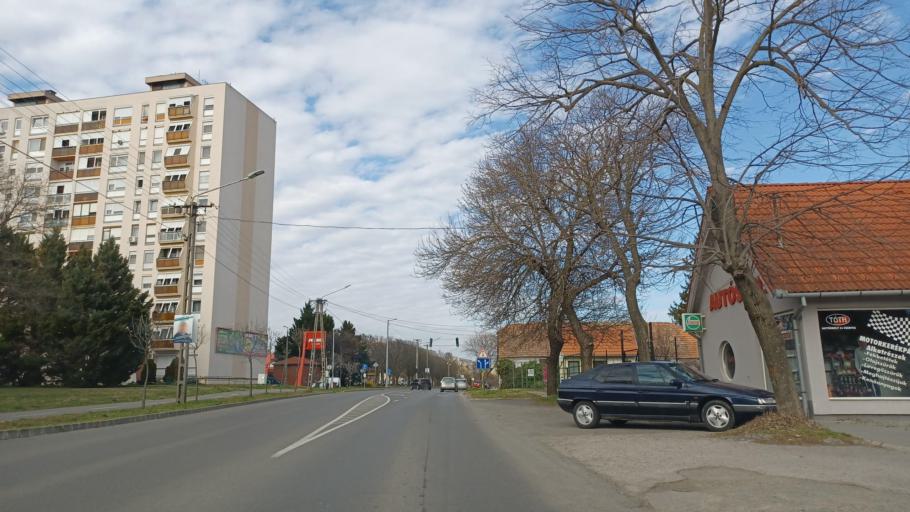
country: HU
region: Tolna
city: Szekszard
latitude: 46.3333
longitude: 18.7001
